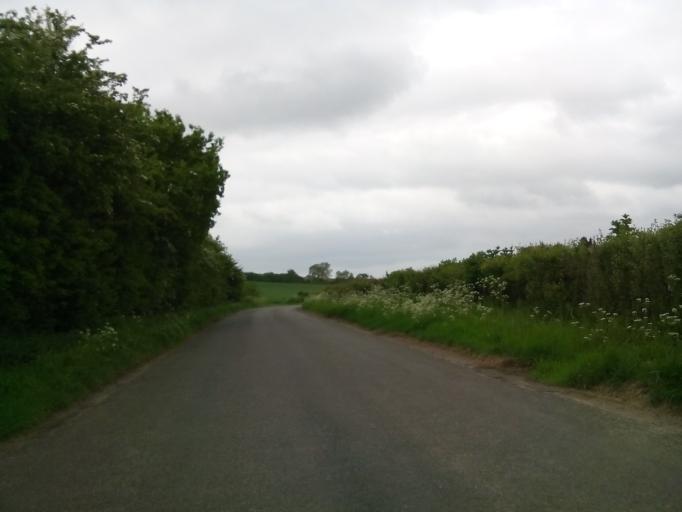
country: GB
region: England
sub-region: Northamptonshire
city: Oundle
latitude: 52.5162
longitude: -0.5300
